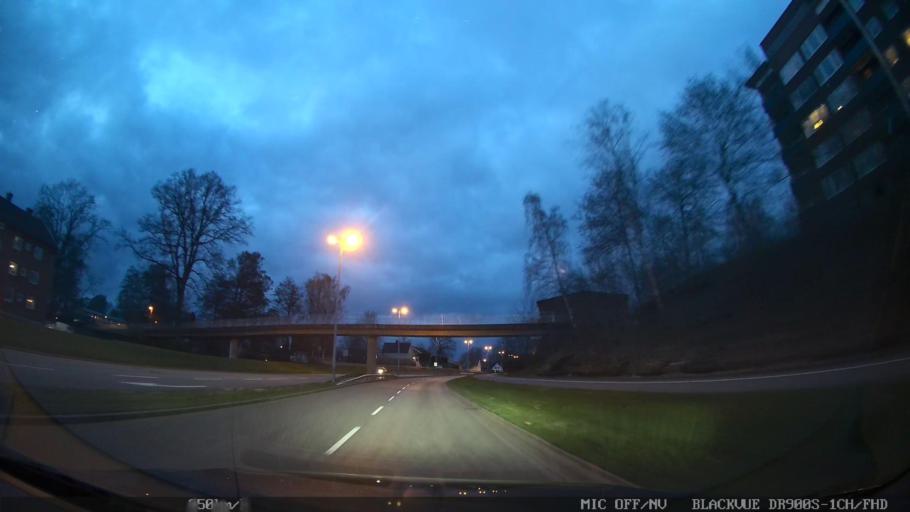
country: SE
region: Skane
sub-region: Hassleholms Kommun
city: Hassleholm
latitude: 56.1588
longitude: 13.7554
